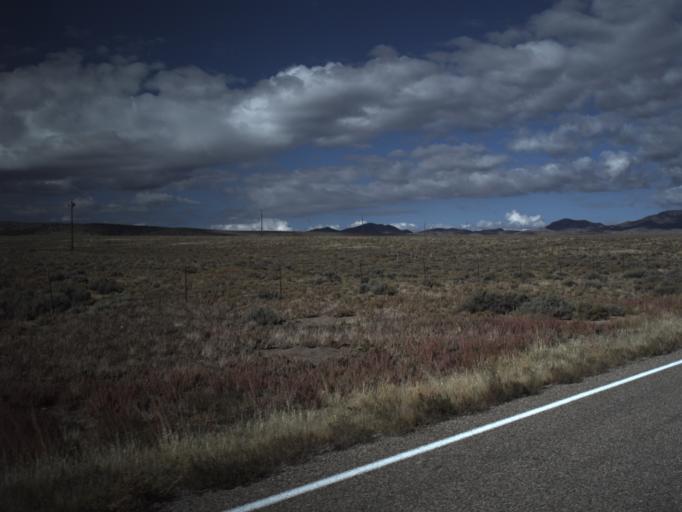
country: US
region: Utah
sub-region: Beaver County
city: Milford
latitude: 38.4267
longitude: -113.1192
